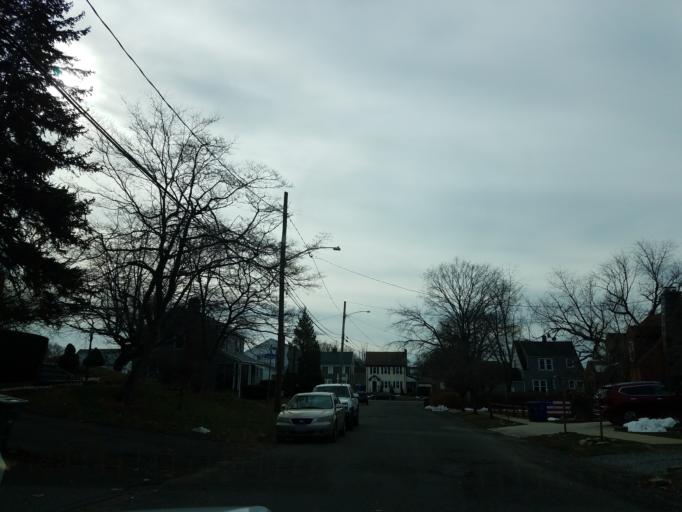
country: US
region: Connecticut
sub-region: Fairfield County
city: Trumbull
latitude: 41.2176
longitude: -73.2114
